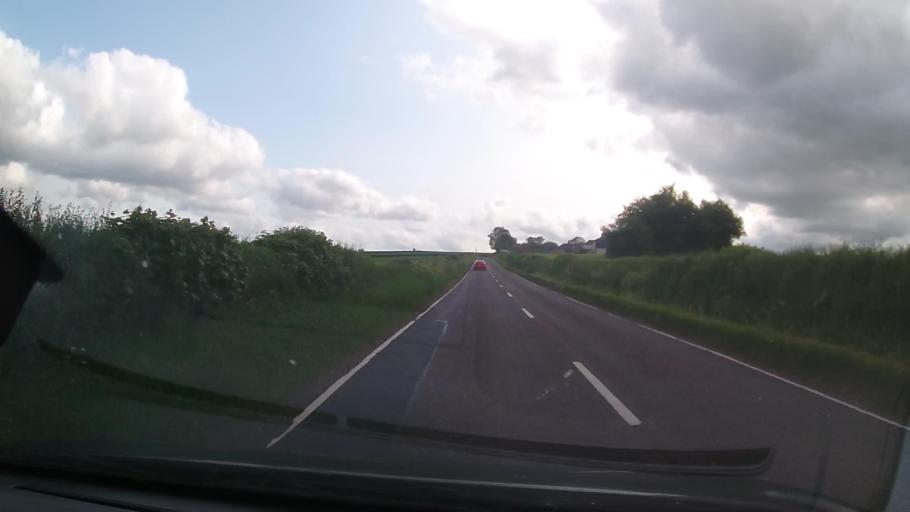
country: GB
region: England
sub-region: Shropshire
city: Clive
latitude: 52.8158
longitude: -2.7439
